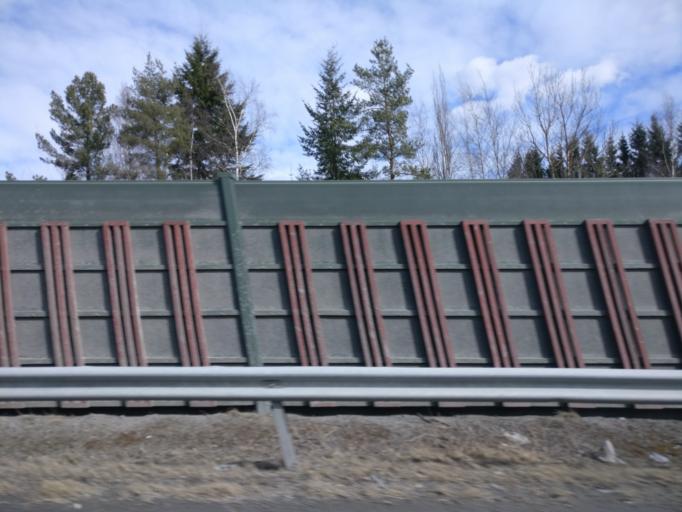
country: FI
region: Pirkanmaa
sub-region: Tampere
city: Lempaeaelae
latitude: 61.3910
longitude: 23.7876
